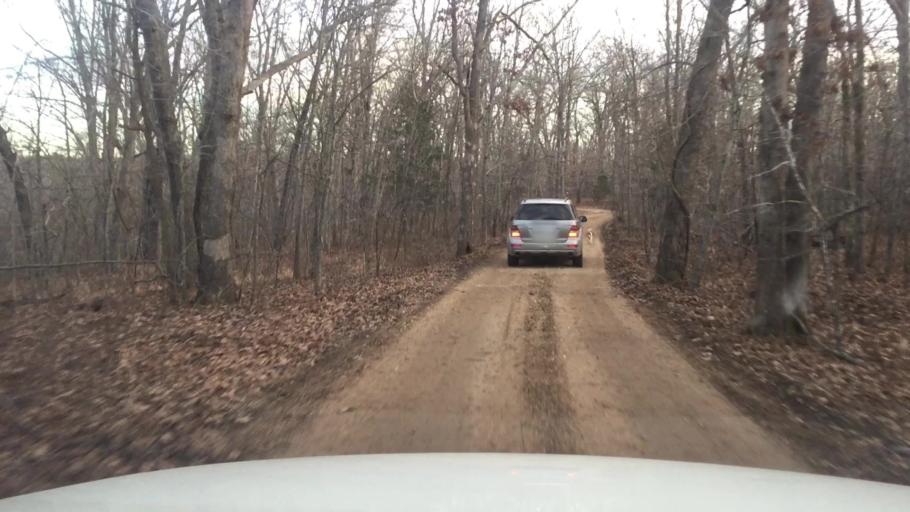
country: US
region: Missouri
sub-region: Camden County
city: Four Seasons
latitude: 38.3108
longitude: -92.7512
